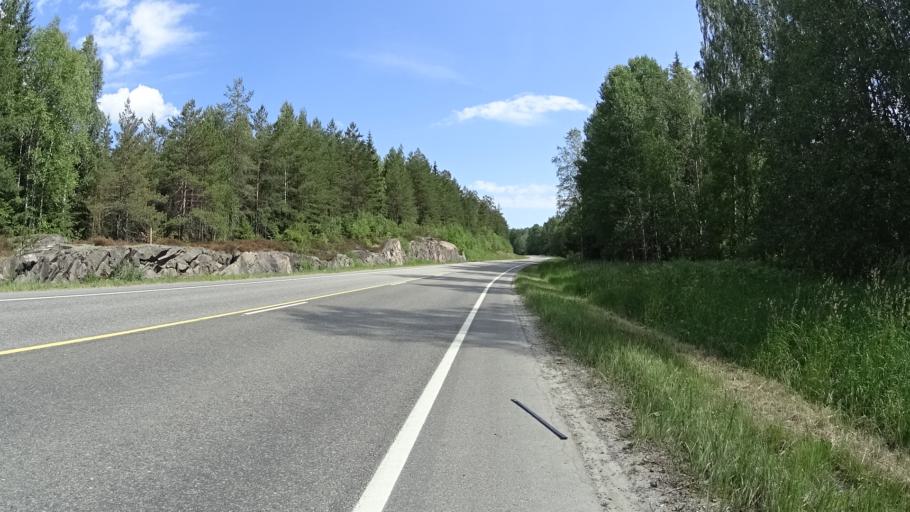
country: FI
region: Uusimaa
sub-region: Raaseporin
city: Pohja
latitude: 60.1019
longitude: 23.5766
